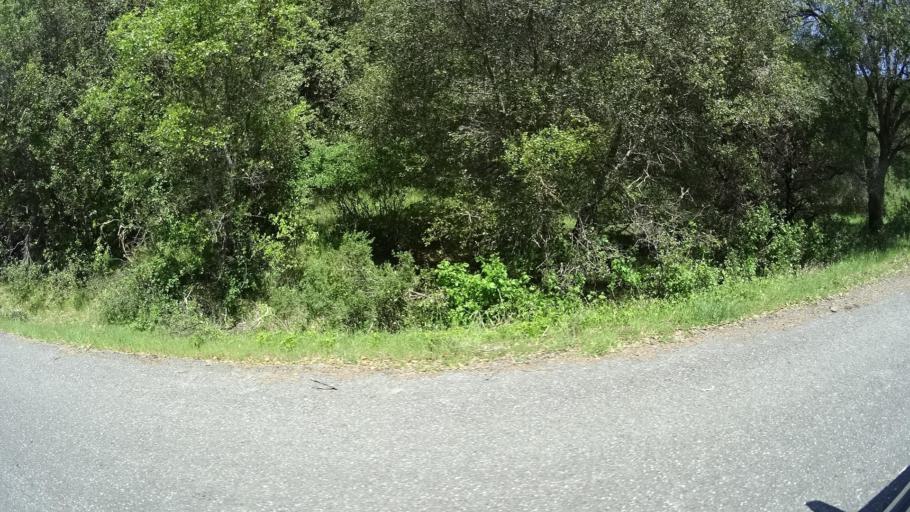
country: US
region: California
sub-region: Humboldt County
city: Redway
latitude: 40.2220
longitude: -123.6358
